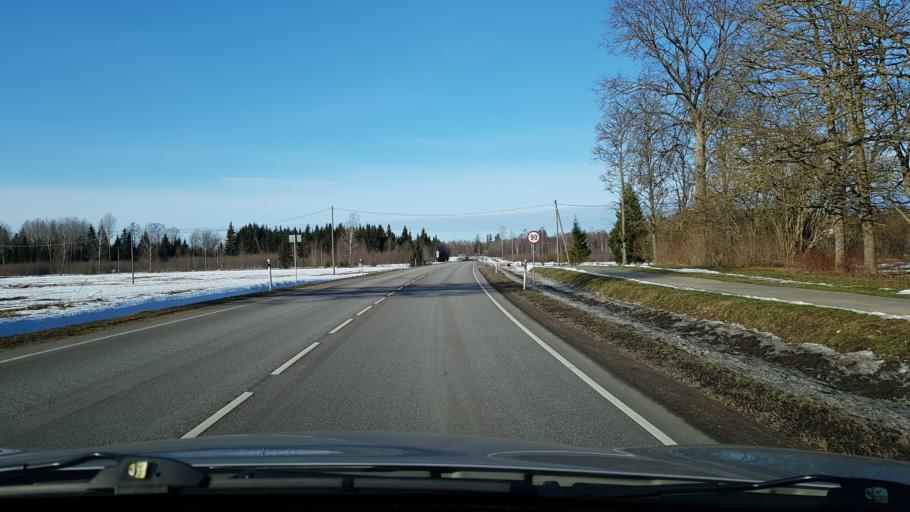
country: EE
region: Viljandimaa
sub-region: Vohma linn
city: Vohma
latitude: 58.6341
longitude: 25.7029
